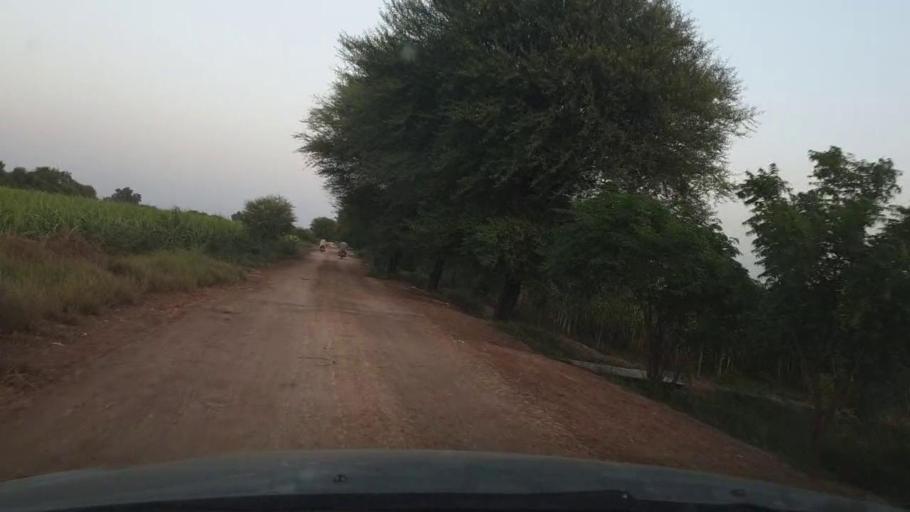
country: PK
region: Sindh
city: Digri
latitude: 25.1113
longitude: 69.0003
